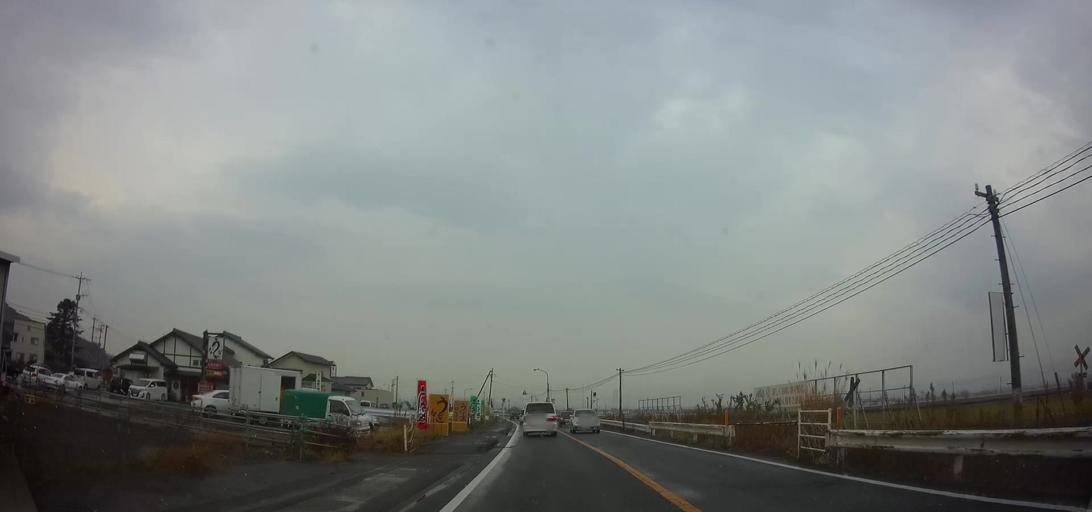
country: JP
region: Nagasaki
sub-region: Isahaya-shi
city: Isahaya
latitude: 32.8378
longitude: 130.1028
